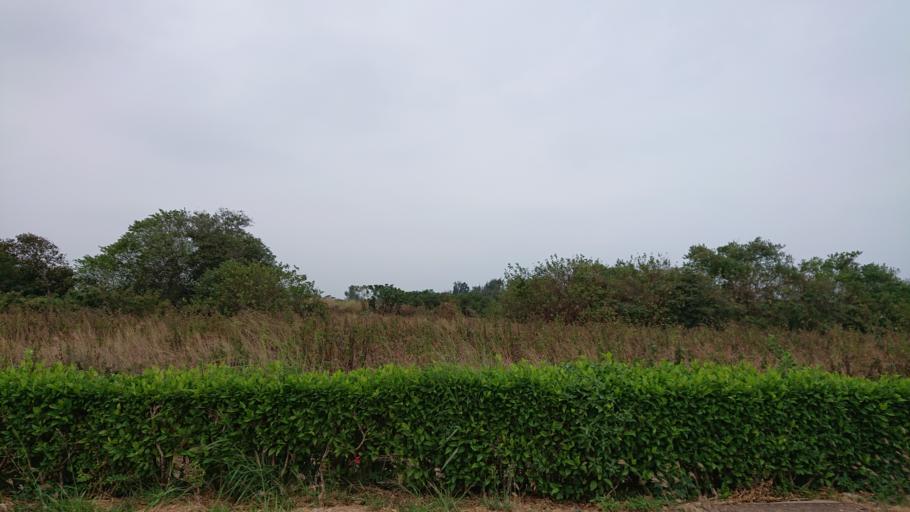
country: TW
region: Fukien
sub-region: Kinmen
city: Jincheng
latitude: 24.4574
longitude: 118.3614
